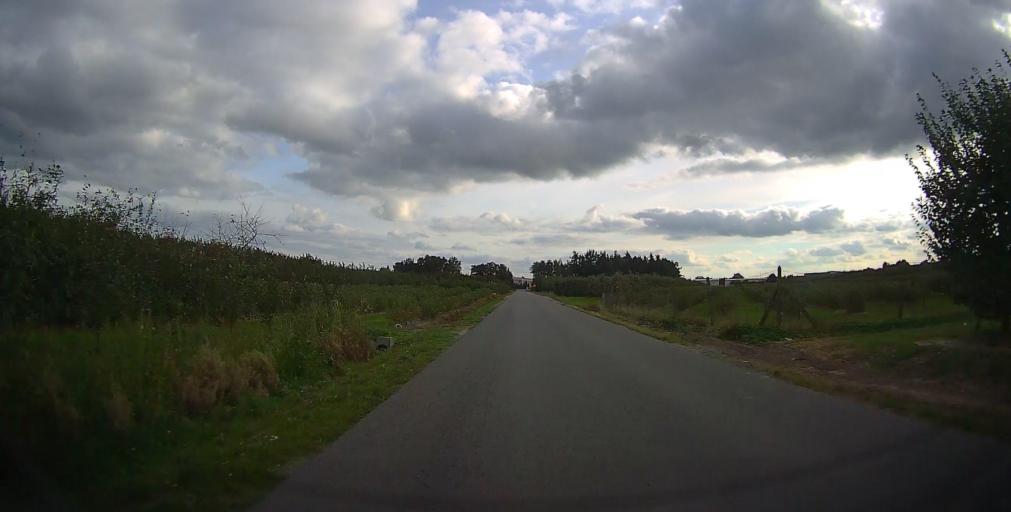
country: PL
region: Masovian Voivodeship
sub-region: Powiat bialobrzeski
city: Promna
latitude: 51.7338
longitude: 20.9648
